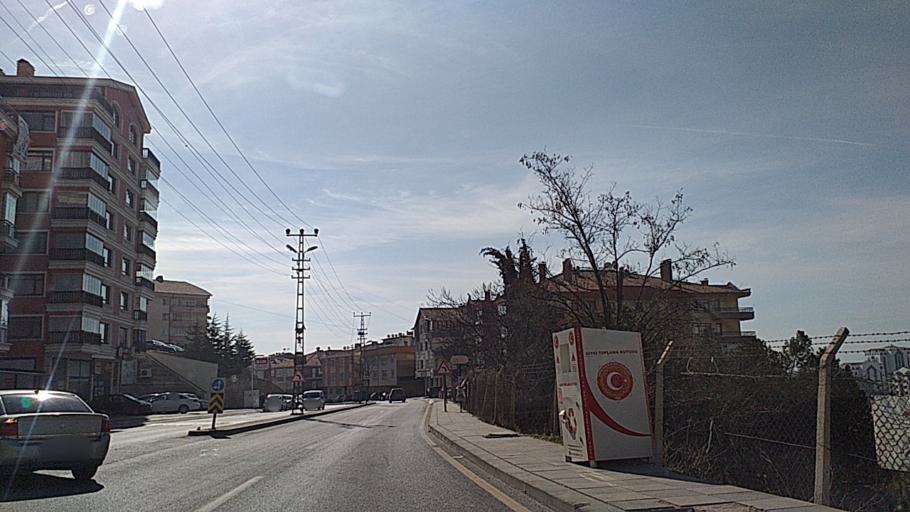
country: TR
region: Ankara
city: Ankara
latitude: 39.9857
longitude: 32.8232
